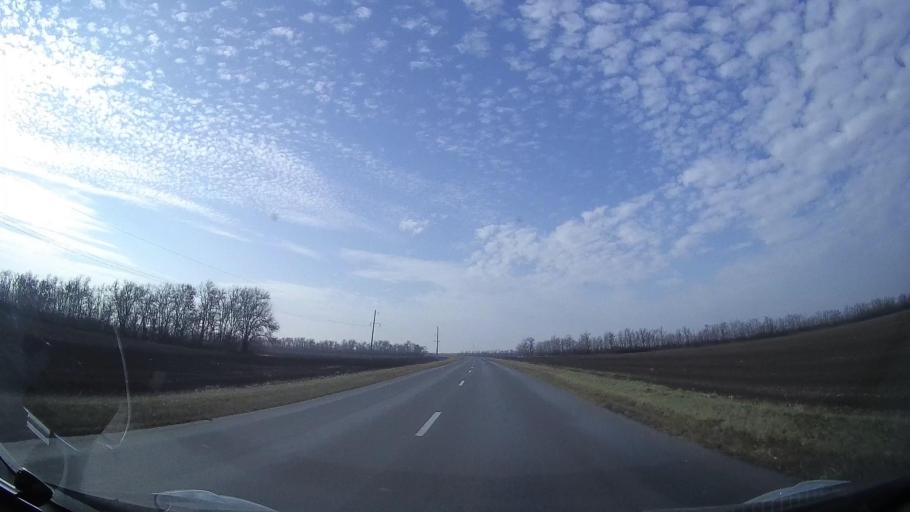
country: RU
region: Rostov
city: Veselyy
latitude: 46.9696
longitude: 40.6574
